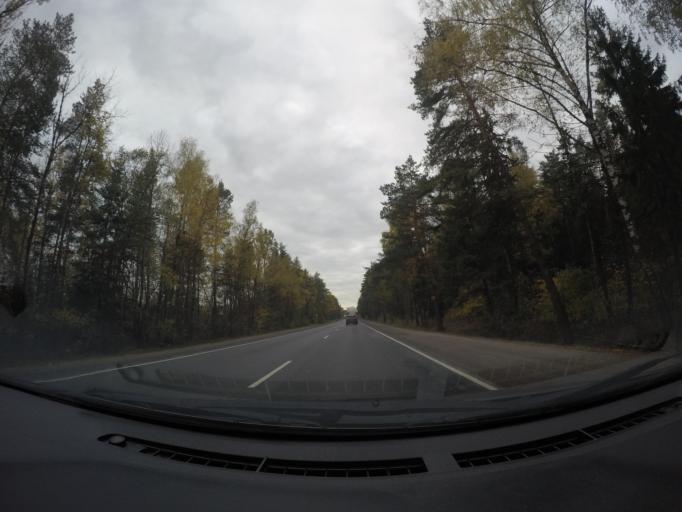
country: RU
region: Moskovskaya
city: Gzhel'
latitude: 55.6497
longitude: 38.3757
